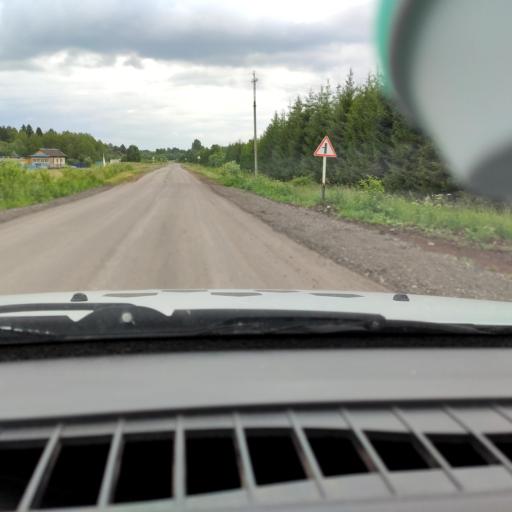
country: RU
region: Perm
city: Uinskoye
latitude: 57.1704
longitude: 56.5639
